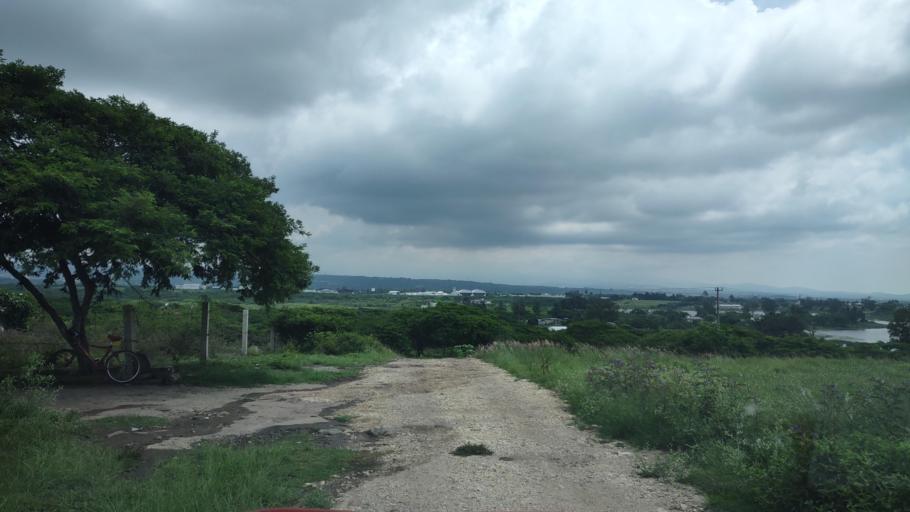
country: MX
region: Veracruz
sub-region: Emiliano Zapata
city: Dos Rios
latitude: 19.4629
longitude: -96.7930
